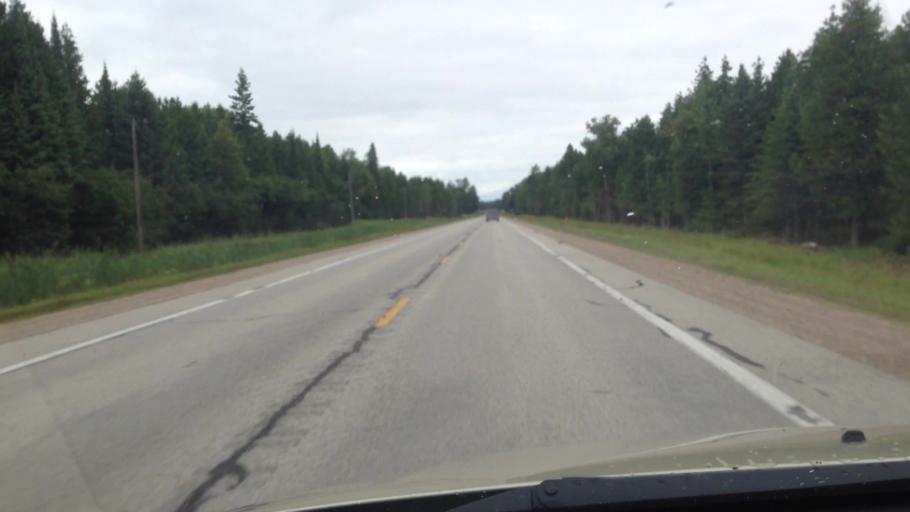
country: US
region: Michigan
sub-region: Delta County
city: Escanaba
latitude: 45.5715
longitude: -87.2522
